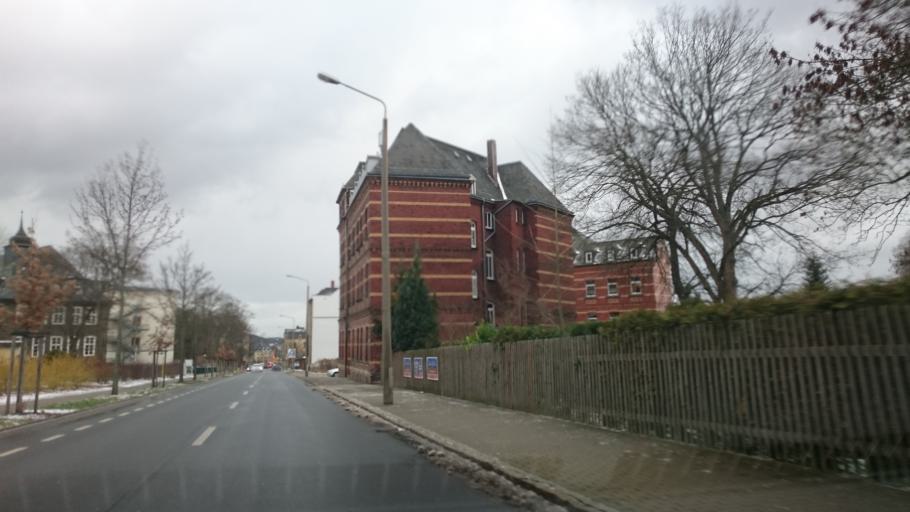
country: DE
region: Saxony
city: Weissenborn
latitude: 50.7225
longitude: 12.4686
